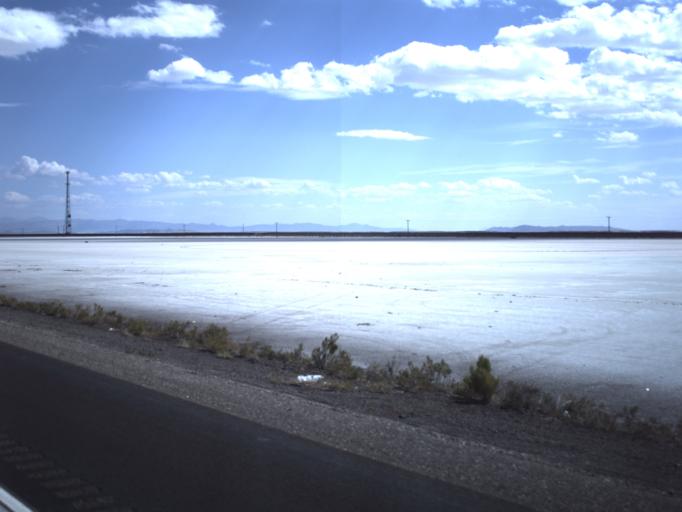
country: US
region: Utah
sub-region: Tooele County
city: Wendover
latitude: 40.7326
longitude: -113.5730
